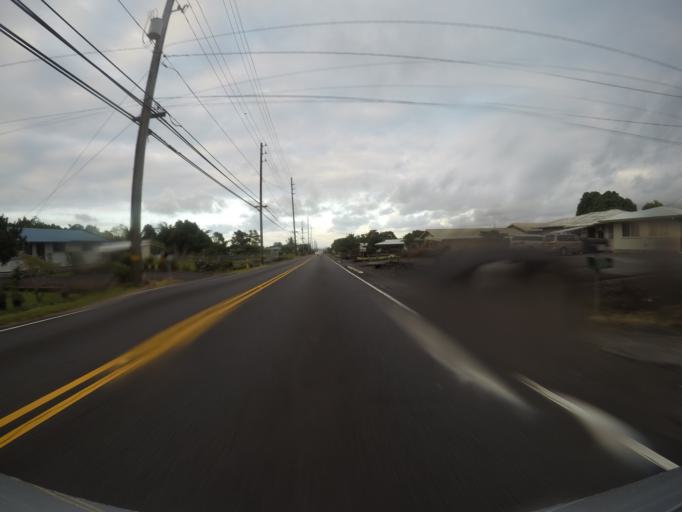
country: US
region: Hawaii
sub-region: Hawaii County
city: Hilo
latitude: 19.6834
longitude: -155.0883
